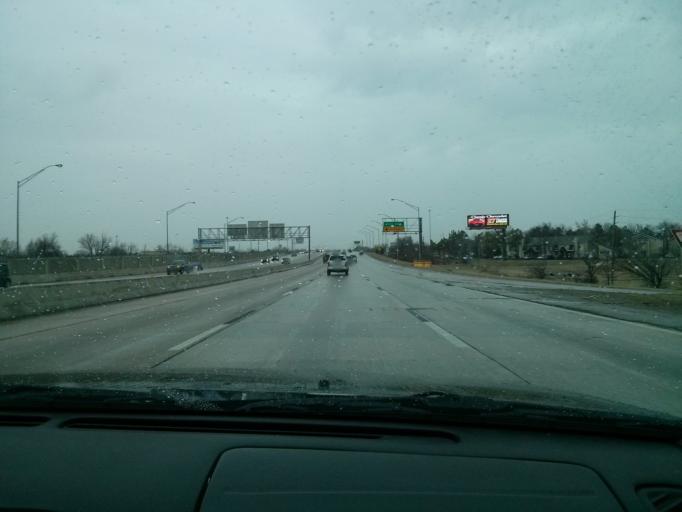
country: US
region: Oklahoma
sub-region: Tulsa County
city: Broken Arrow
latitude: 36.1005
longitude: -95.8596
